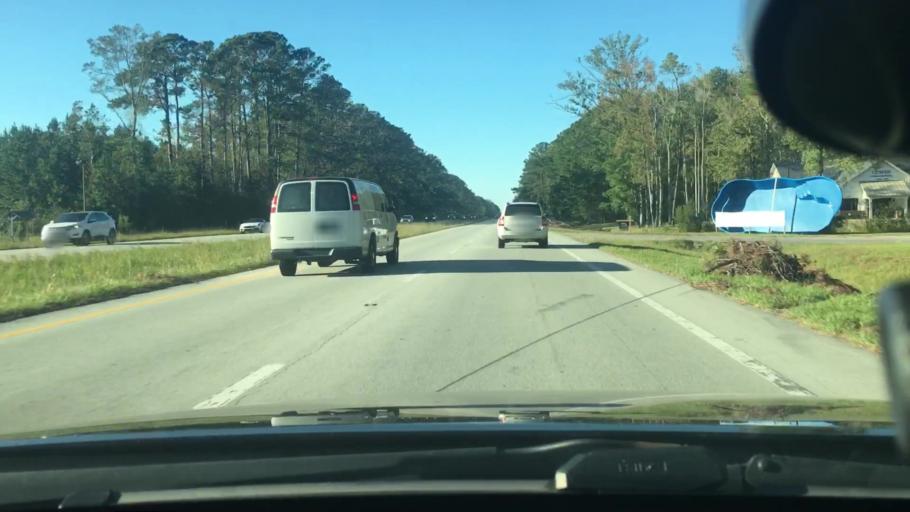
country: US
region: North Carolina
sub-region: Craven County
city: Fairfield Harbour
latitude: 35.0163
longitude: -76.9953
